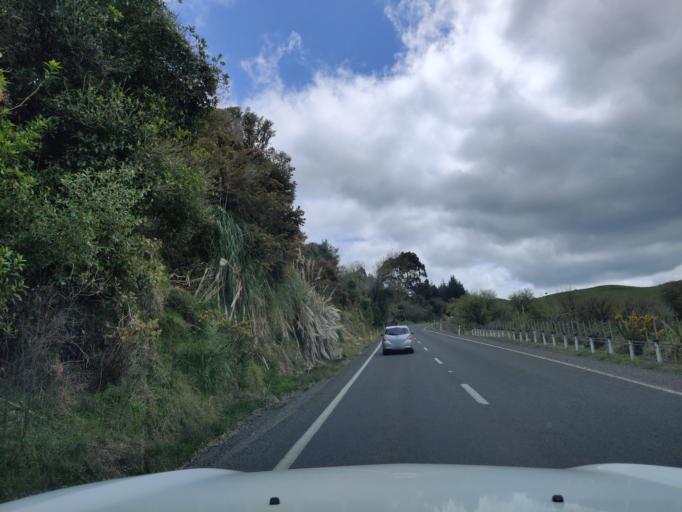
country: NZ
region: Manawatu-Wanganui
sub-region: Wanganui District
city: Wanganui
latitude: -39.7881
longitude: 175.2428
